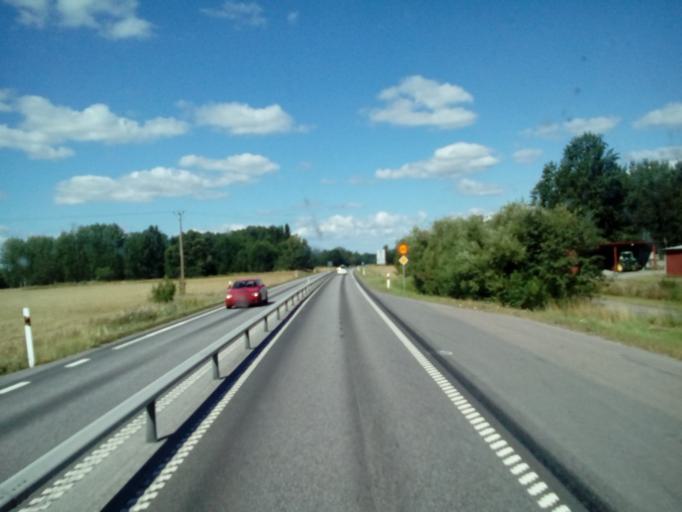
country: SE
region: OEstergoetland
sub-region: Linkopings Kommun
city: Malmslatt
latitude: 58.3587
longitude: 15.5458
